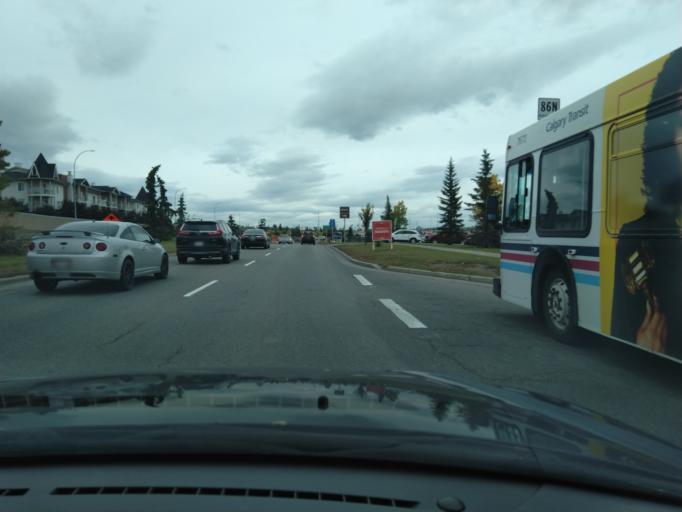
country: CA
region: Alberta
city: Calgary
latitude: 51.1578
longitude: -114.0699
